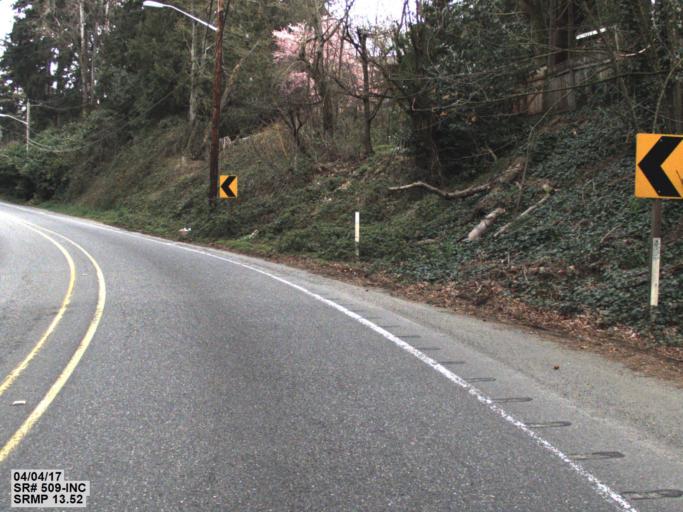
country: US
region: Washington
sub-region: King County
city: Federal Way
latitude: 47.3304
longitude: -122.3228
